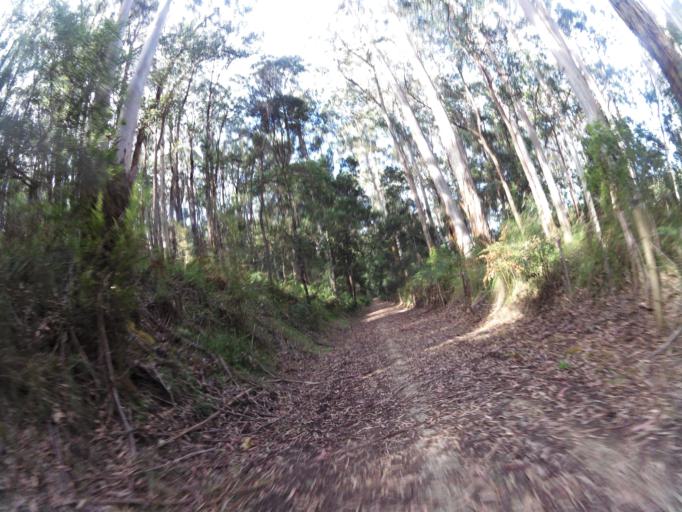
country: AU
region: Victoria
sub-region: Colac-Otway
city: Colac
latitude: -38.4927
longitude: 143.7370
